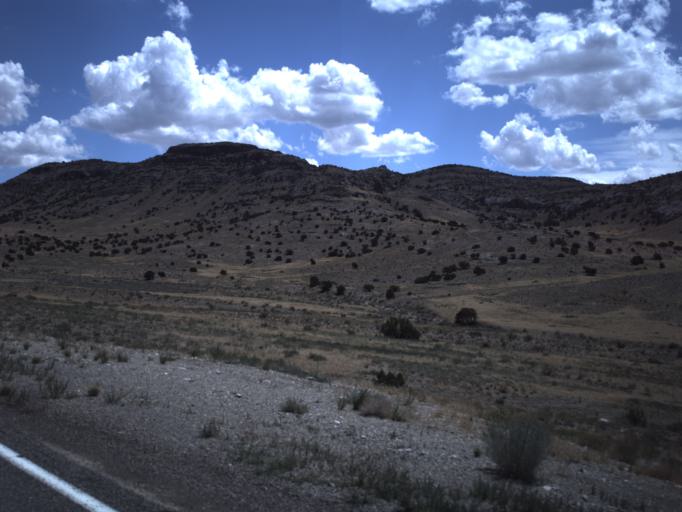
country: US
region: Utah
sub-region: Beaver County
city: Milford
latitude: 39.0712
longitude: -113.6528
